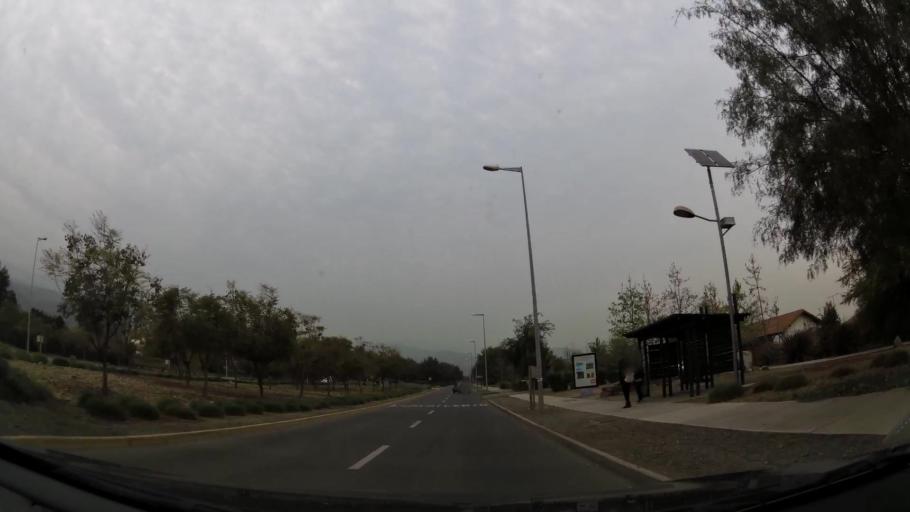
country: CL
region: Santiago Metropolitan
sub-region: Provincia de Chacabuco
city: Chicureo Abajo
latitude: -33.2597
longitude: -70.6269
